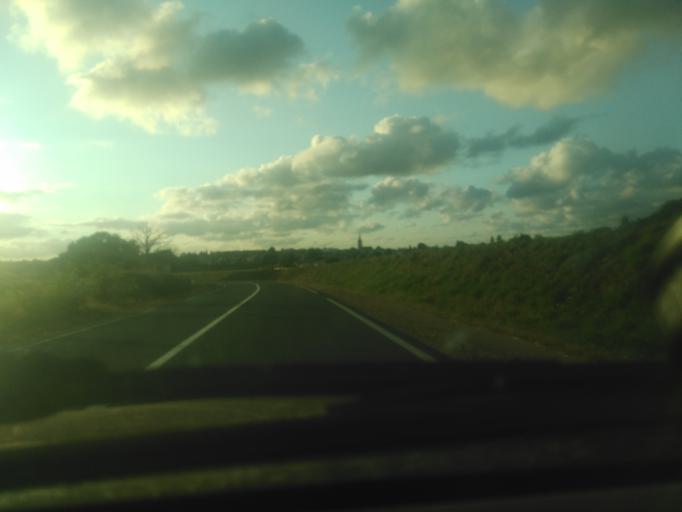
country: FR
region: Pays de la Loire
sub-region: Departement de la Vendee
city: La Ferriere
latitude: 46.7049
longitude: -1.3106
